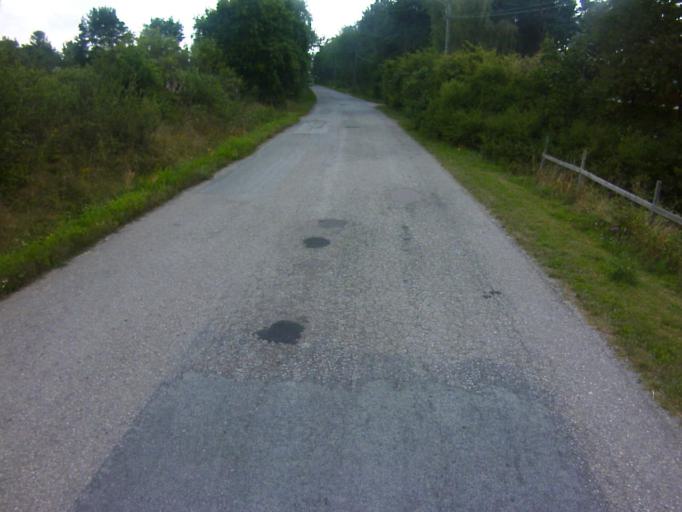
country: SE
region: Blekinge
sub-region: Solvesborgs Kommun
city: Soelvesborg
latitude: 56.0169
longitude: 14.6778
